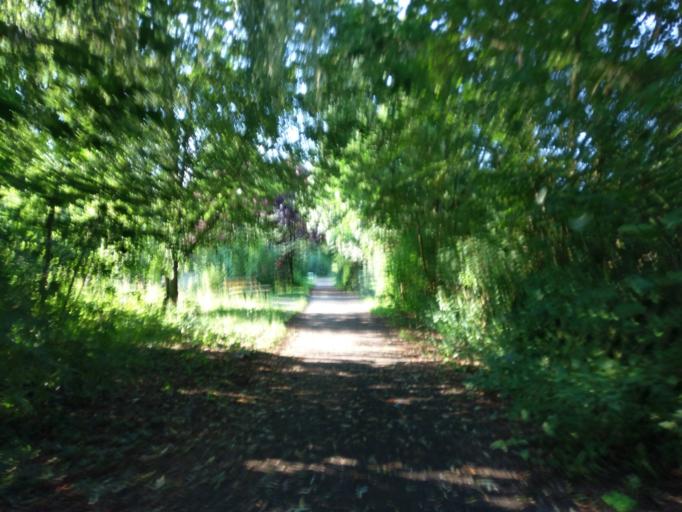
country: DE
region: Berlin
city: Zehlendorf Bezirk
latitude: 52.4228
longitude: 13.2443
